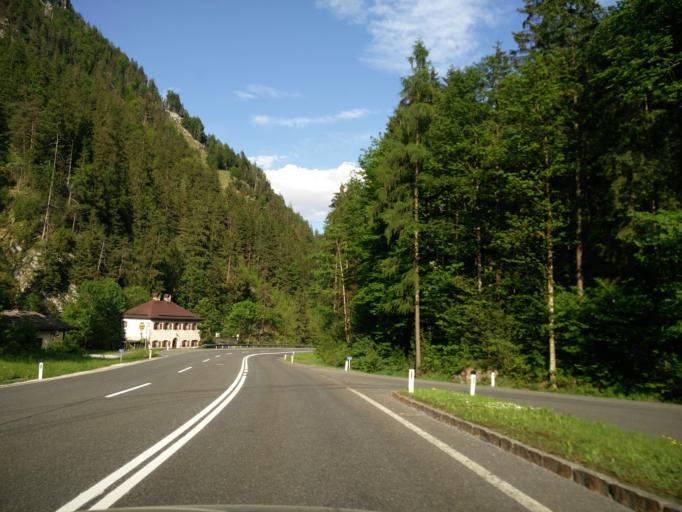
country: AT
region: Salzburg
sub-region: Politischer Bezirk Zell am See
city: Lofer
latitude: 47.5794
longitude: 12.6631
